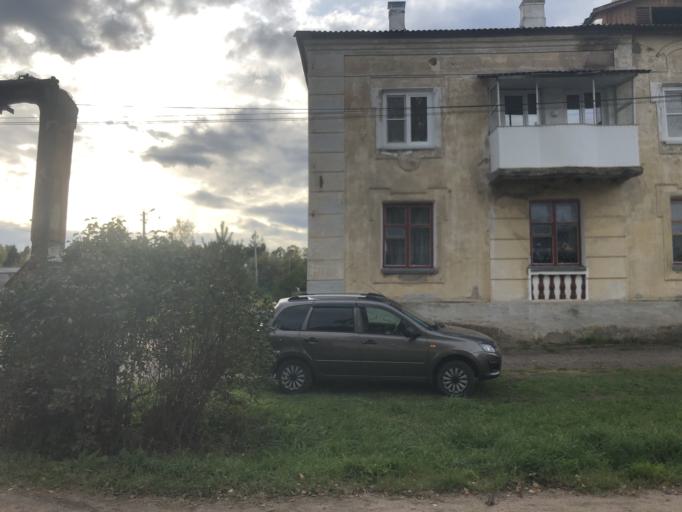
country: RU
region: Tverskaya
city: Rzhev
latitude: 56.2536
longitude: 34.2930
